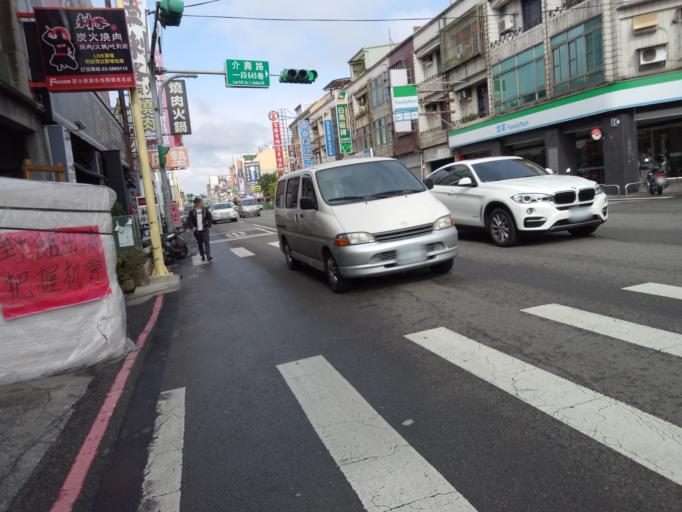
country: TW
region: Taiwan
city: Taoyuan City
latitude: 24.9668
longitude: 121.3010
